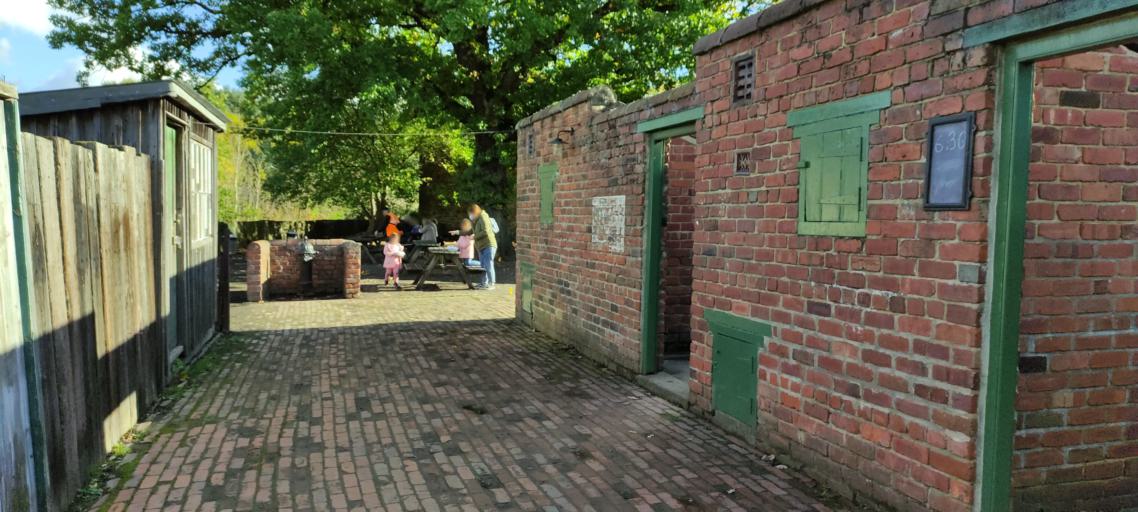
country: GB
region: England
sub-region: County Durham
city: Stanley
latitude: 54.8840
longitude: -1.6613
